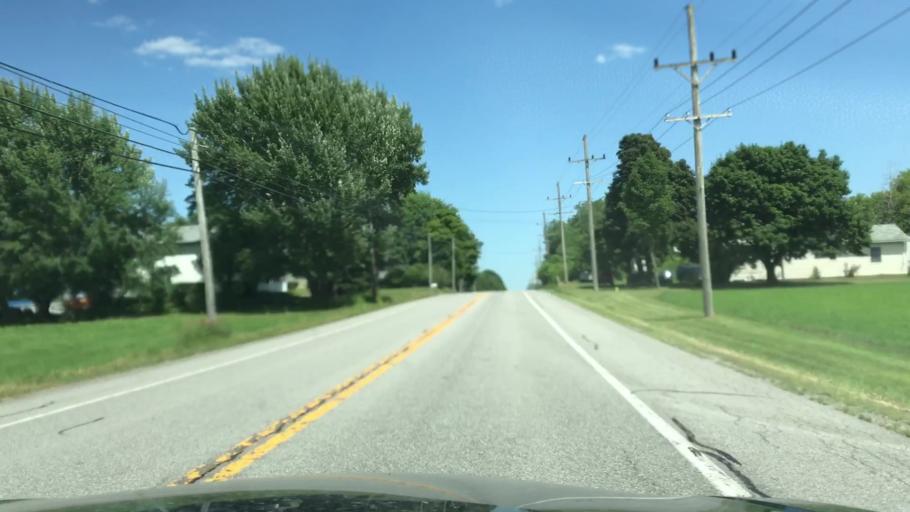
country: US
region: New York
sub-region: Wyoming County
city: Perry
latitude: 42.7480
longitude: -78.0150
